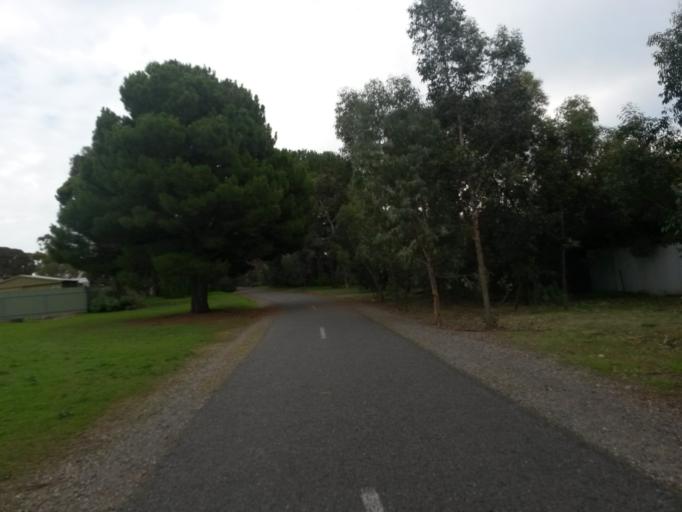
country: AU
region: South Australia
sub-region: Onkaparinga
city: McLaren Vale
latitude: -35.2137
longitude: 138.5333
